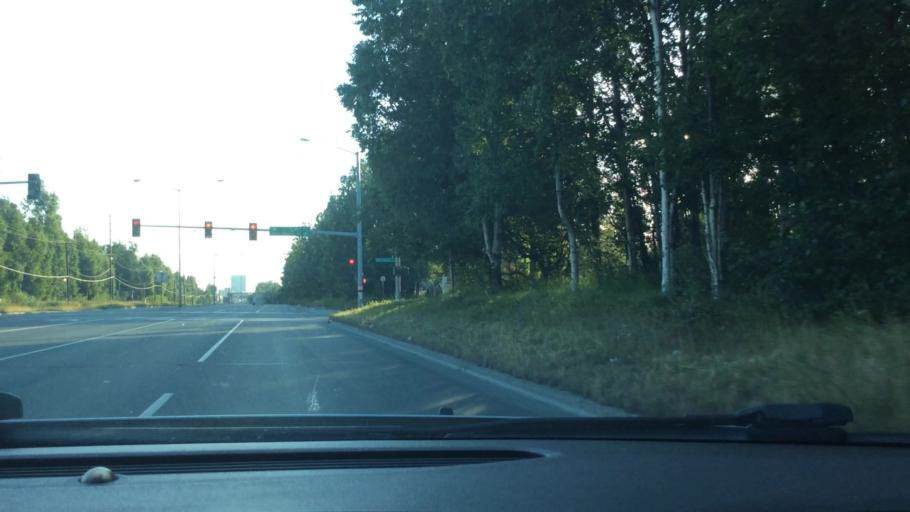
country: US
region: Alaska
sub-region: Anchorage Municipality
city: Anchorage
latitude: 61.1955
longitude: -149.8445
